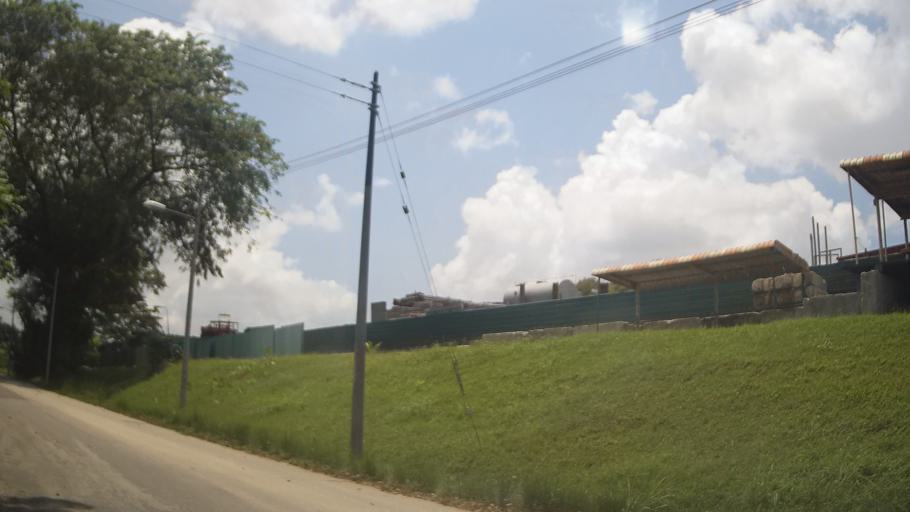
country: MY
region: Johor
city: Kampung Pasir Gudang Baru
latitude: 1.3978
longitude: 103.8625
